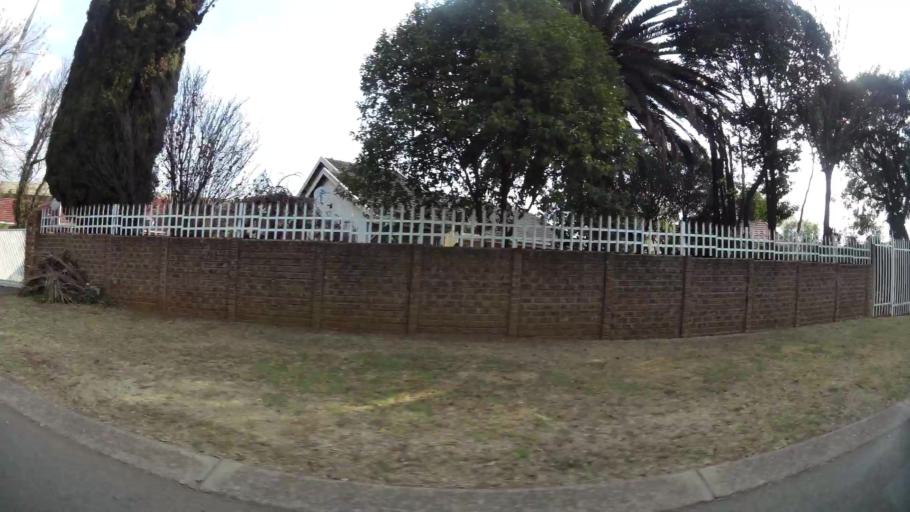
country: ZA
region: Gauteng
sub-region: City of Johannesburg Metropolitan Municipality
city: Modderfontein
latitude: -26.1136
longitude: 28.1996
